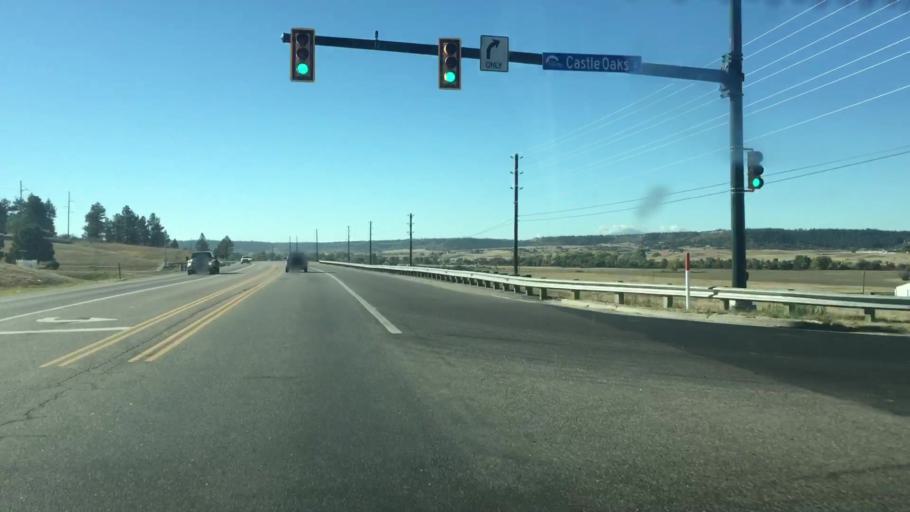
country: US
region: Colorado
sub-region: Douglas County
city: The Pinery
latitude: 39.4167
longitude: -104.7612
